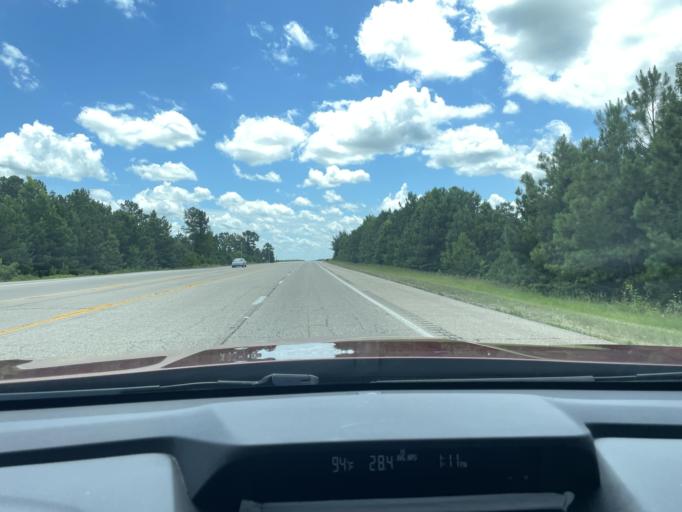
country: US
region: Arkansas
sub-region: Drew County
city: Monticello
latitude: 33.7081
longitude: -91.8079
